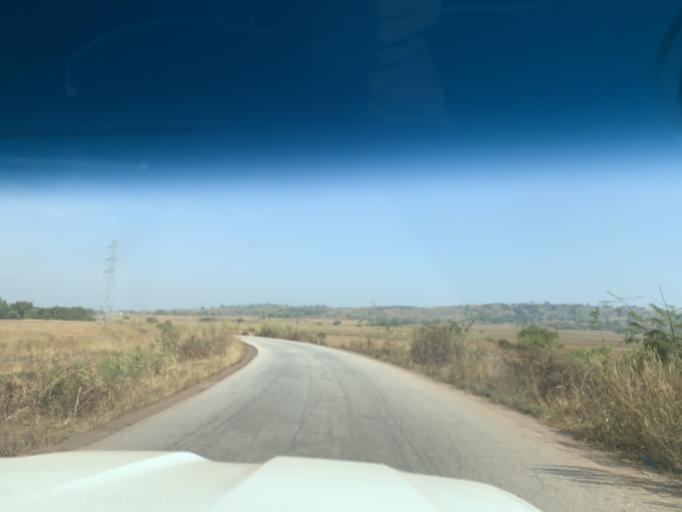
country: GN
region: Kindia
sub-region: Kindia
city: Kindia
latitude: 10.0367
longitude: -12.6635
